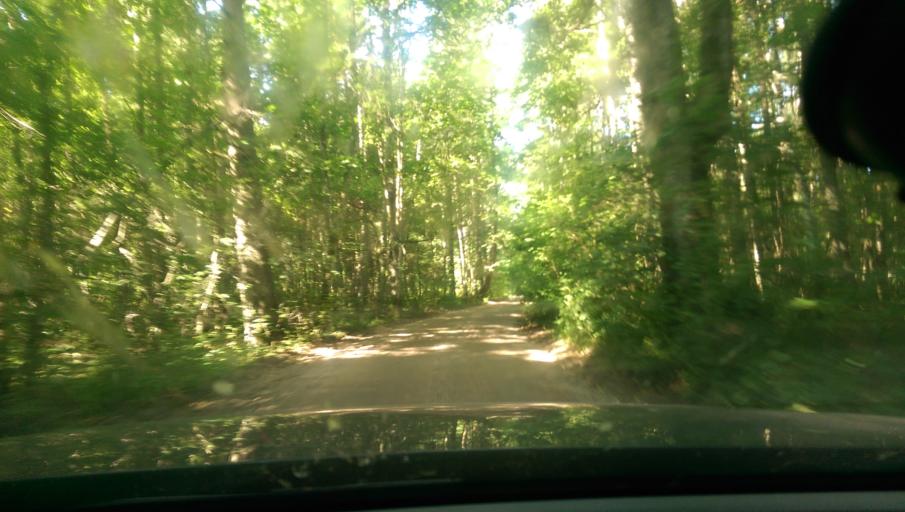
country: LT
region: Klaipedos apskritis
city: Gargzdai
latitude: 55.6518
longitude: 21.3307
